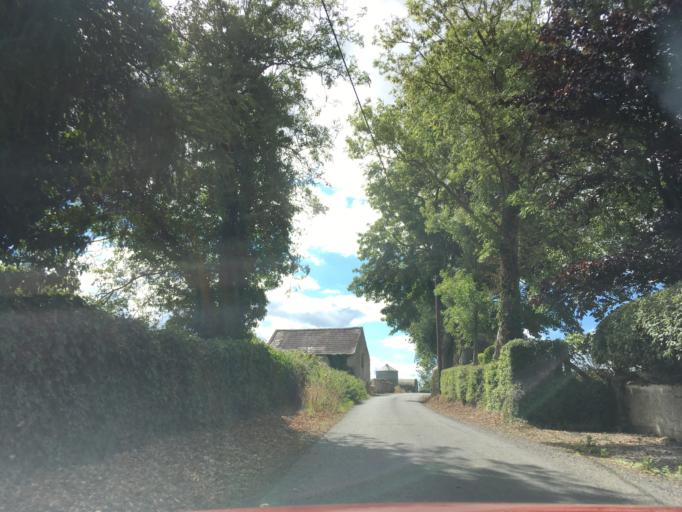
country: IE
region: Munster
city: Cashel
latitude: 52.4962
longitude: -7.9058
